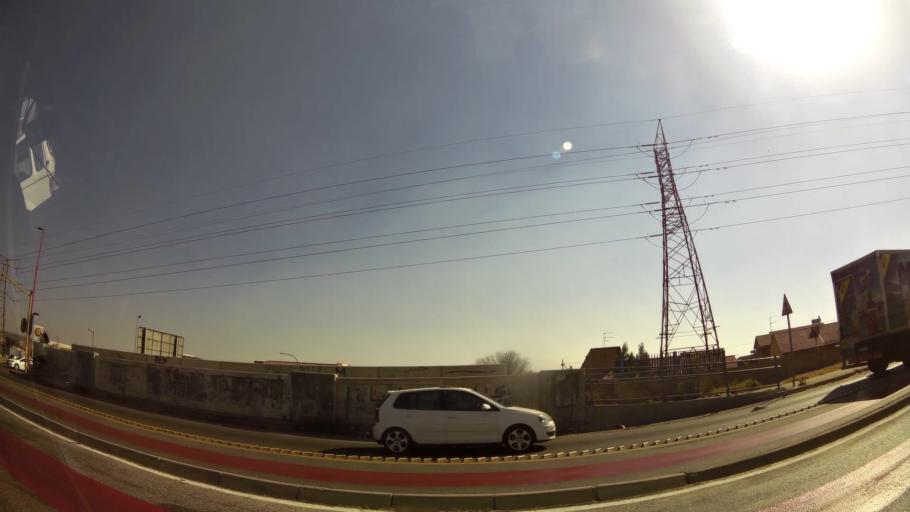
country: ZA
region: Gauteng
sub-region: City of Johannesburg Metropolitan Municipality
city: Johannesburg
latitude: -26.1896
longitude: 27.9697
